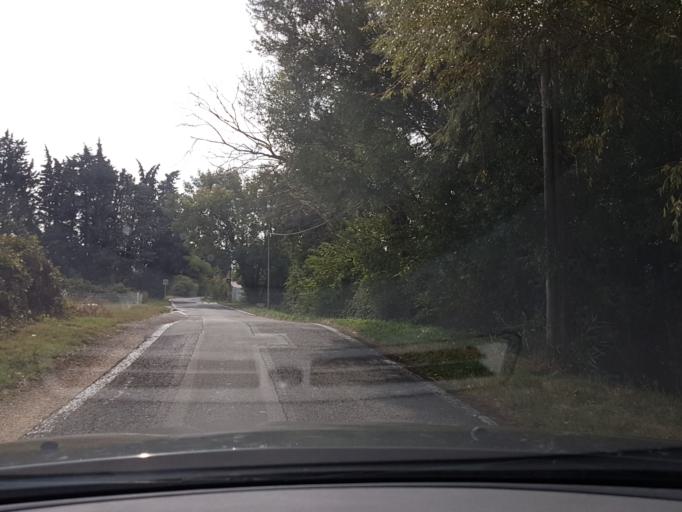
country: FR
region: Provence-Alpes-Cote d'Azur
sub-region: Departement du Vaucluse
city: Saint-Saturnin-les-Avignon
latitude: 43.9631
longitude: 4.9406
